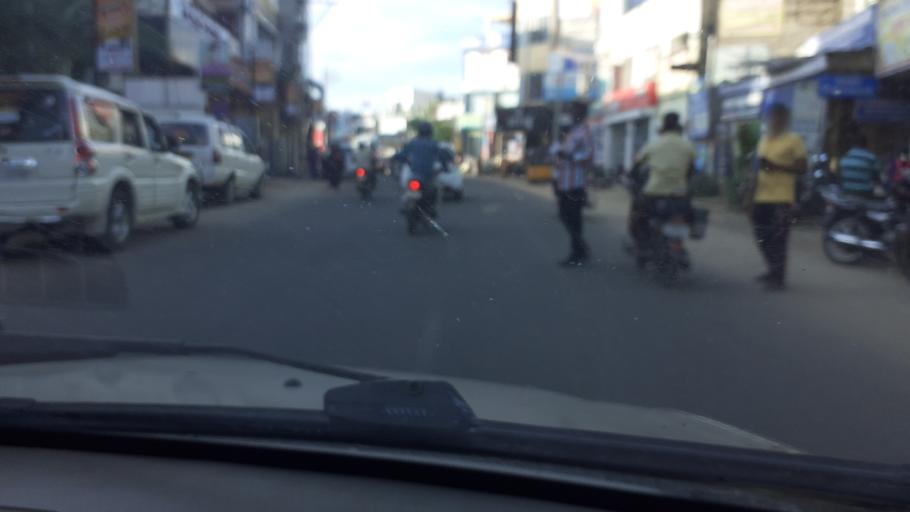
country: IN
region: Tamil Nadu
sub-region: Tirunelveli Kattabo
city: Tirunelveli
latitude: 8.7248
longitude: 77.7317
